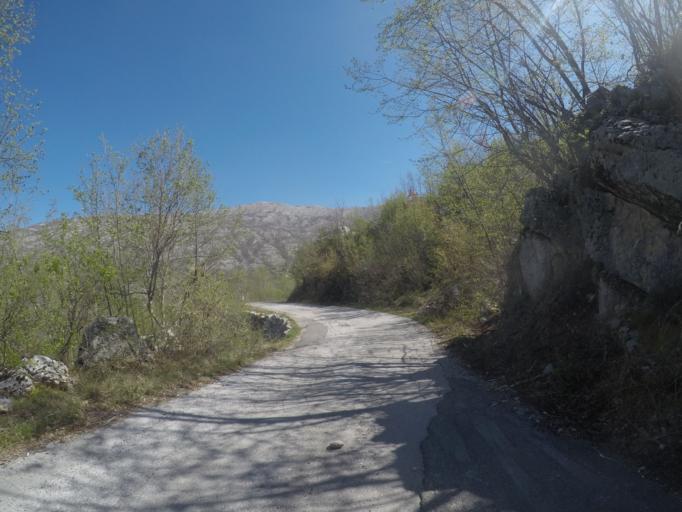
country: ME
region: Danilovgrad
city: Danilovgrad
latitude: 42.5404
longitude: 18.9993
